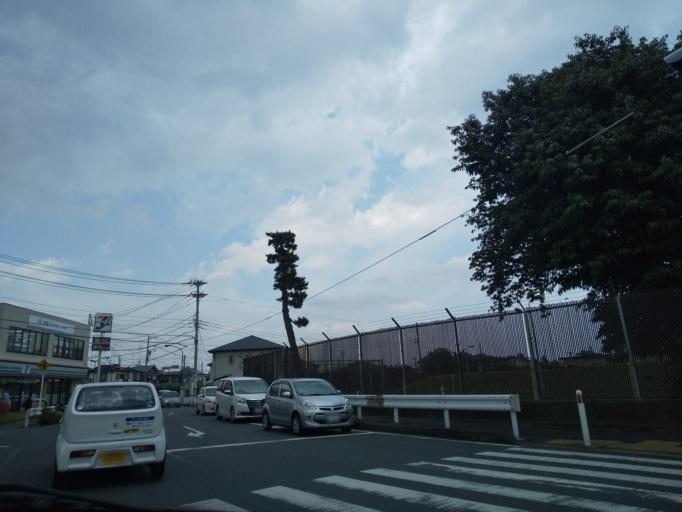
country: JP
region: Kanagawa
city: Zama
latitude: 35.5239
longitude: 139.4119
